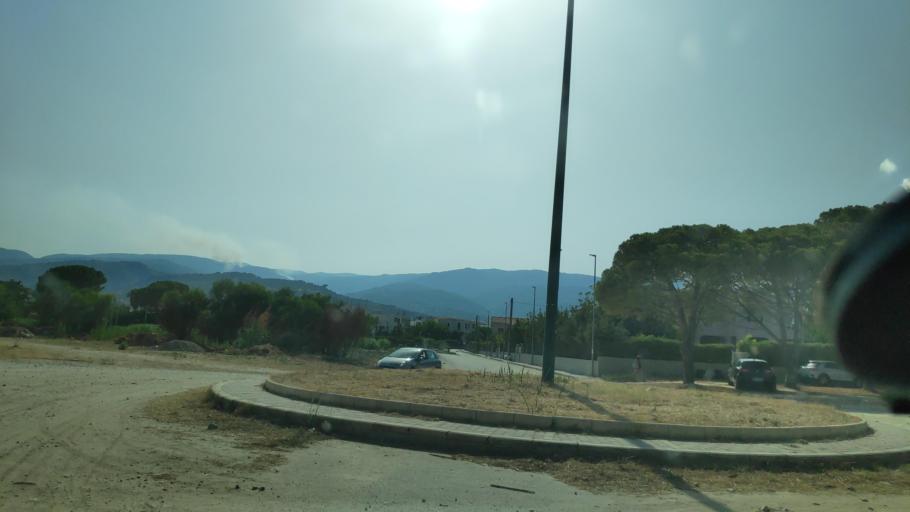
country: IT
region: Calabria
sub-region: Provincia di Catanzaro
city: Isca Marina
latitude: 38.6021
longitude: 16.5659
